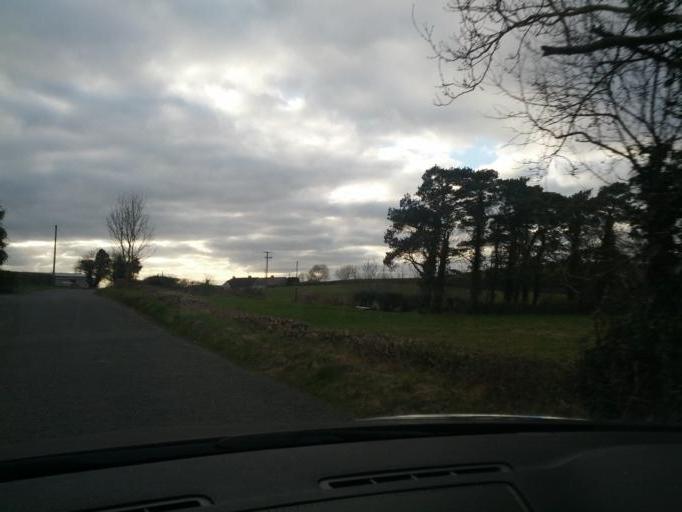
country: IE
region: Leinster
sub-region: Uibh Fhaili
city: Ferbane
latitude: 53.3276
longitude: -7.8813
